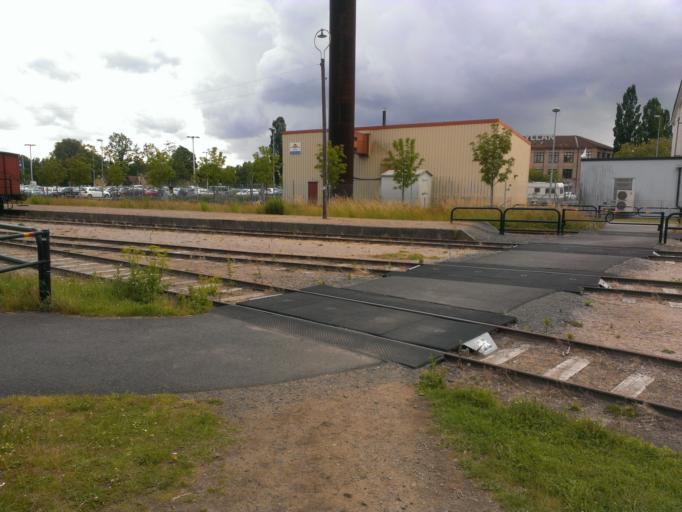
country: SE
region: Skane
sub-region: Kristianstads Kommun
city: Kristianstad
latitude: 56.0234
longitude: 14.1611
